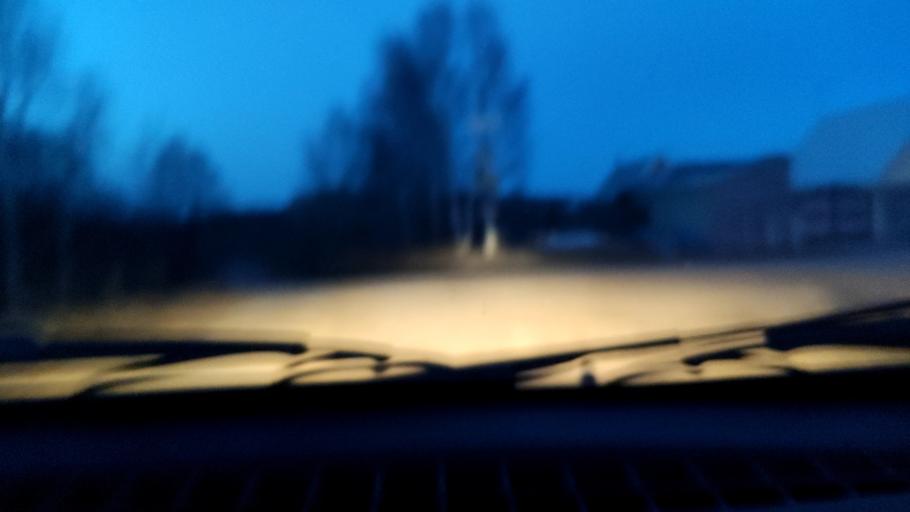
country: RU
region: Bashkortostan
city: Iglino
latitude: 54.7965
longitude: 56.3129
